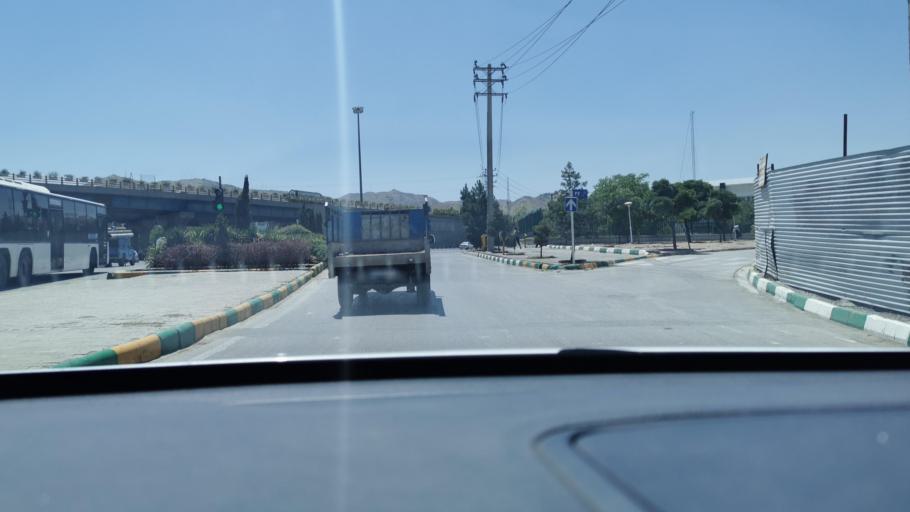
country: IR
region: Razavi Khorasan
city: Mashhad
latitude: 36.2570
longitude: 59.5992
